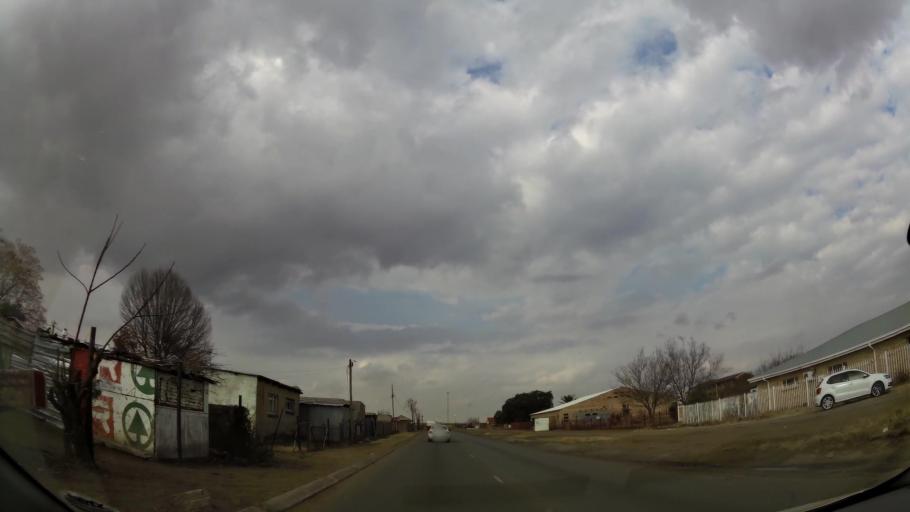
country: ZA
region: Orange Free State
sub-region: Fezile Dabi District Municipality
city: Sasolburg
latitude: -26.8413
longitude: 27.8493
